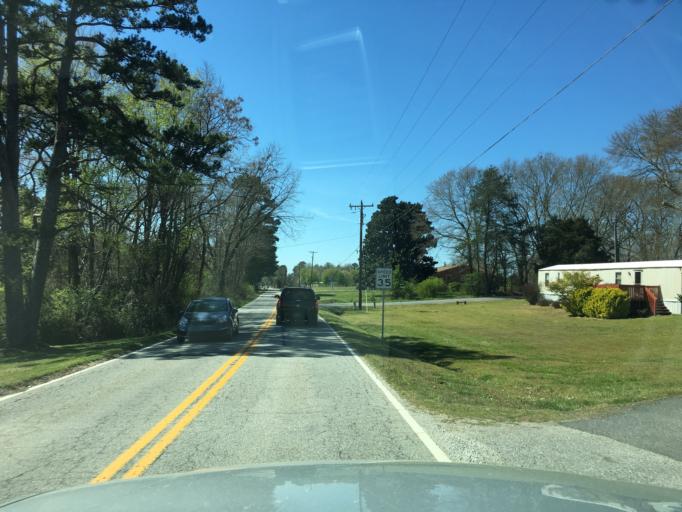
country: US
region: South Carolina
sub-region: Spartanburg County
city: Roebuck
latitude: 34.8840
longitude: -81.9826
